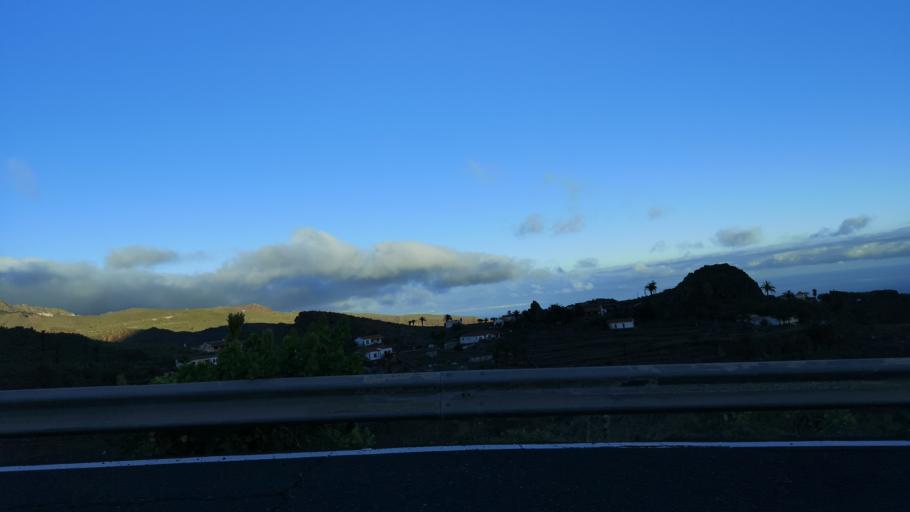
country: ES
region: Canary Islands
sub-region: Provincia de Santa Cruz de Tenerife
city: Alajero
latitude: 28.0570
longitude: -17.2277
